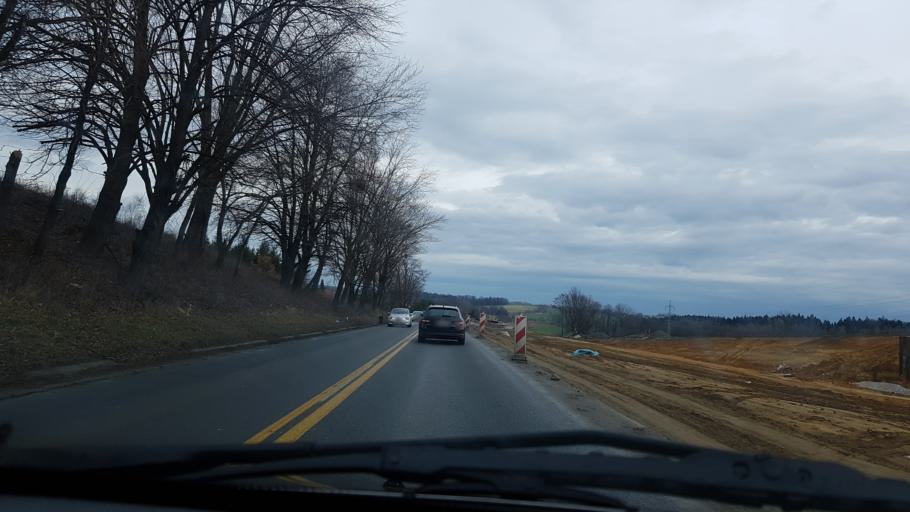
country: CZ
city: Rybi
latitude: 49.6261
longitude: 18.0810
